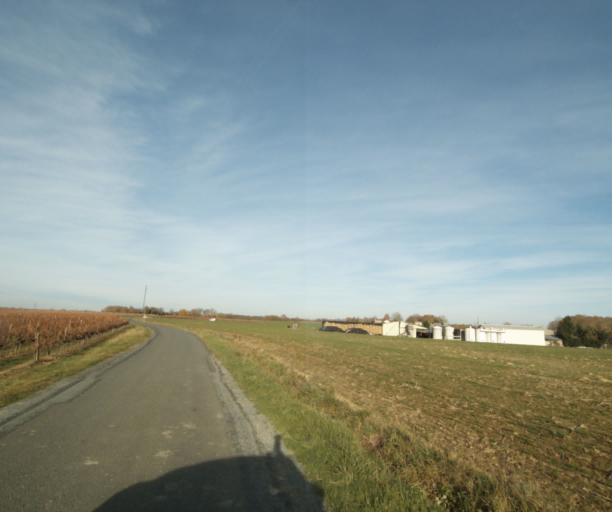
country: FR
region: Poitou-Charentes
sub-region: Departement de la Charente-Maritime
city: Chaniers
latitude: 45.7388
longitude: -0.5215
